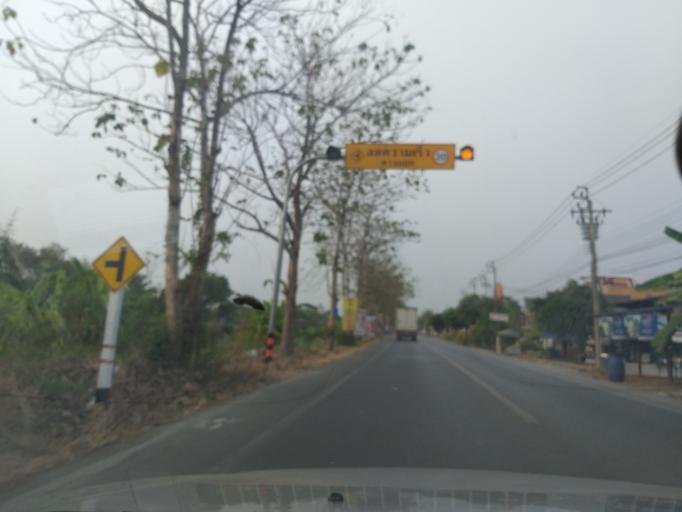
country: TH
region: Bangkok
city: Nong Chok
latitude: 13.9025
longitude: 100.8889
